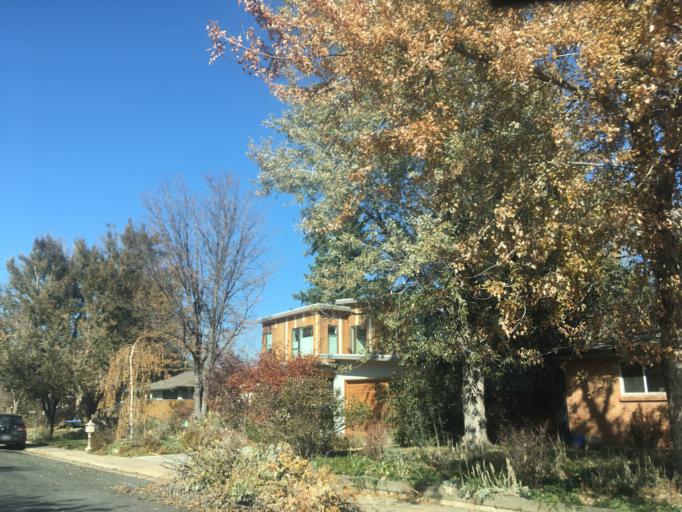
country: US
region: Colorado
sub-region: Boulder County
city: Boulder
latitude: 39.9876
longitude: -105.2423
